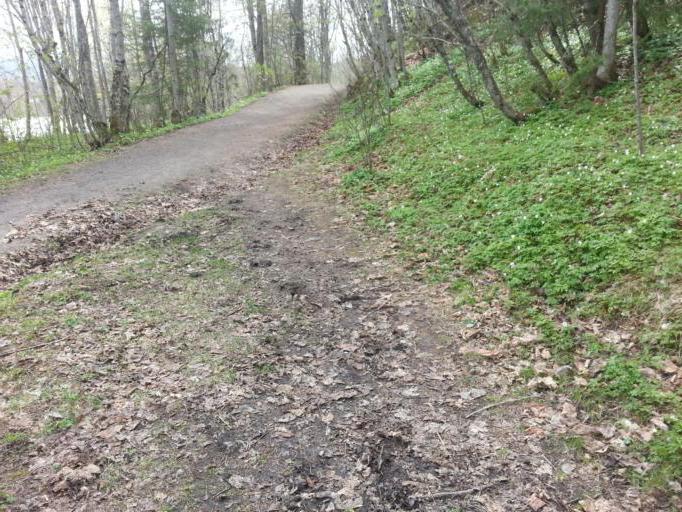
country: NO
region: Sor-Trondelag
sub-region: Trondheim
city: Trondheim
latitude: 63.3905
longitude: 10.3437
